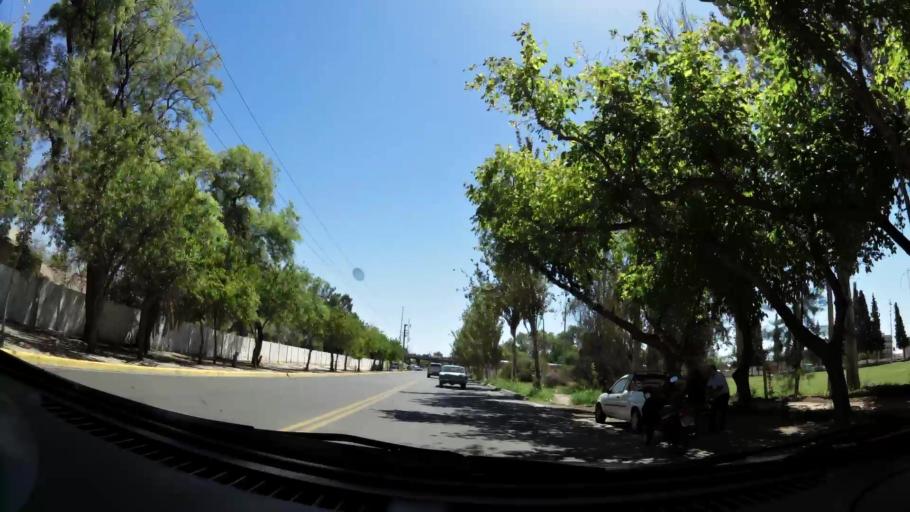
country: AR
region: San Juan
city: San Juan
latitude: -31.5271
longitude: -68.5549
